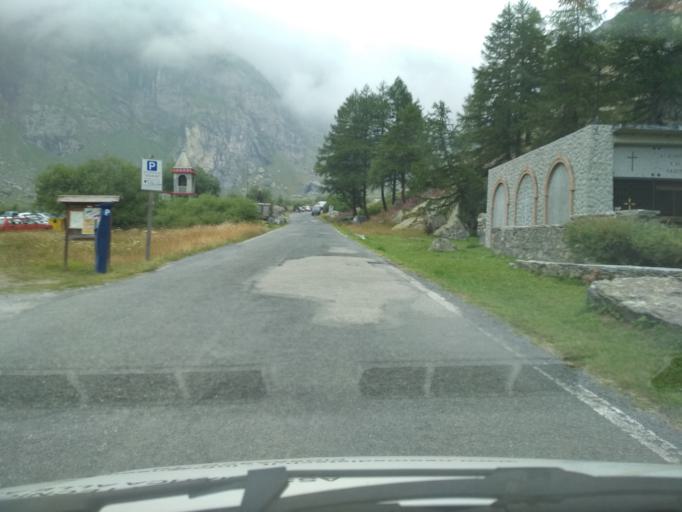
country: IT
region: Piedmont
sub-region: Provincia di Torino
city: Balme
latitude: 45.3057
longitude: 7.1684
